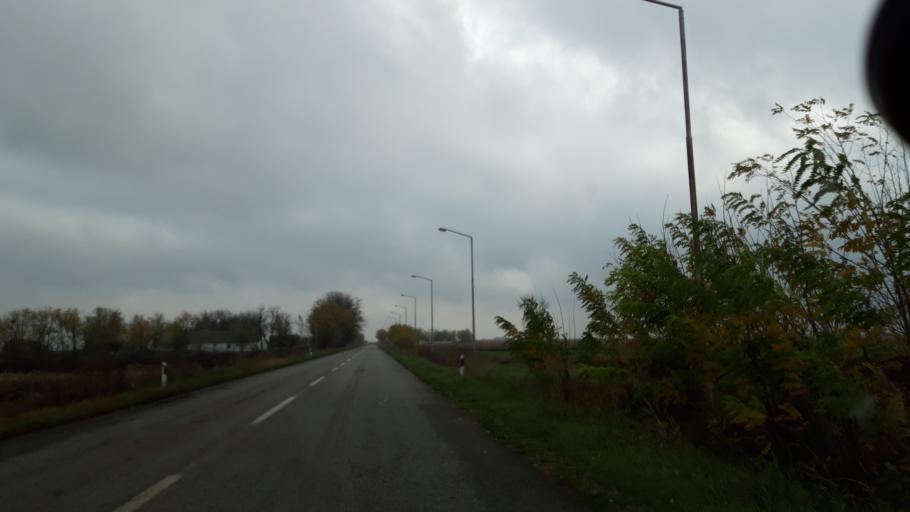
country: RS
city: Backo Gradiste
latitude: 45.4998
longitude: 19.9448
